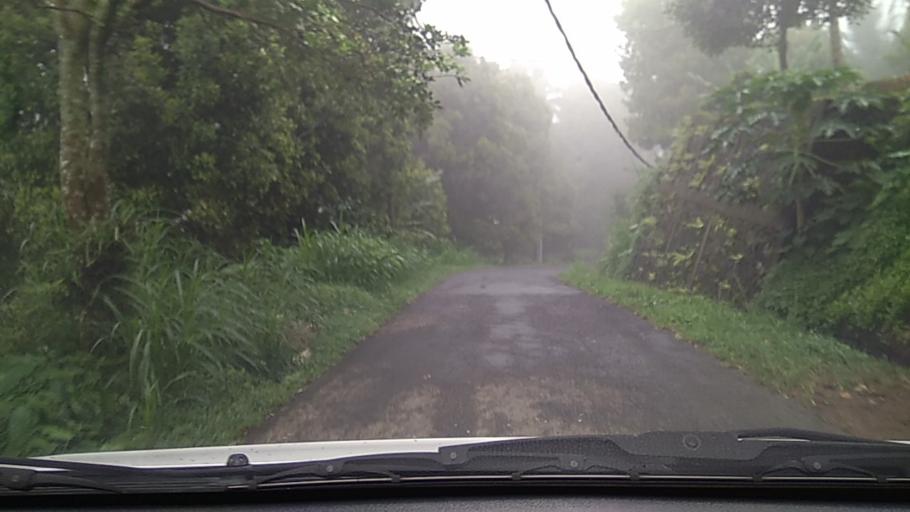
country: ID
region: Bali
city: Banjar Ambengan
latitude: -8.1994
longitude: 115.1764
